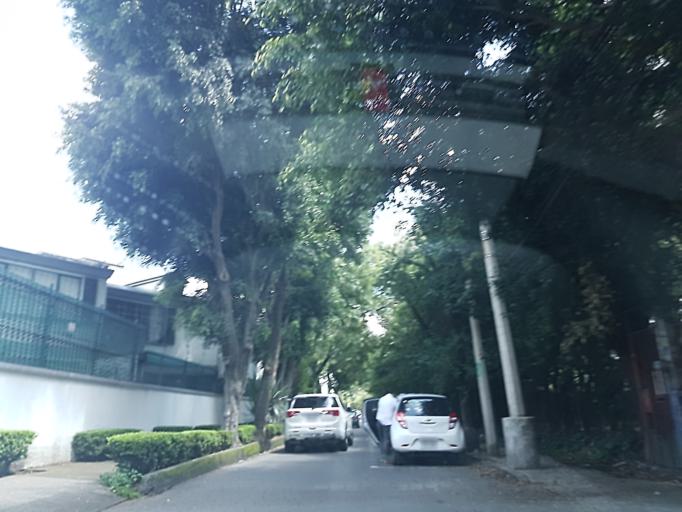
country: MX
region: Mexico City
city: Alvaro Obregon
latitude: 19.3527
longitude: -99.1847
